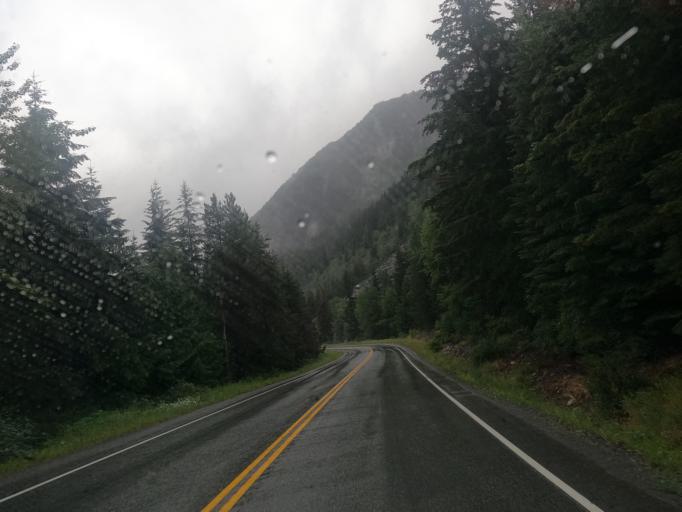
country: CA
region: British Columbia
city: Lillooet
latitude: 50.5288
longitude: -122.1585
